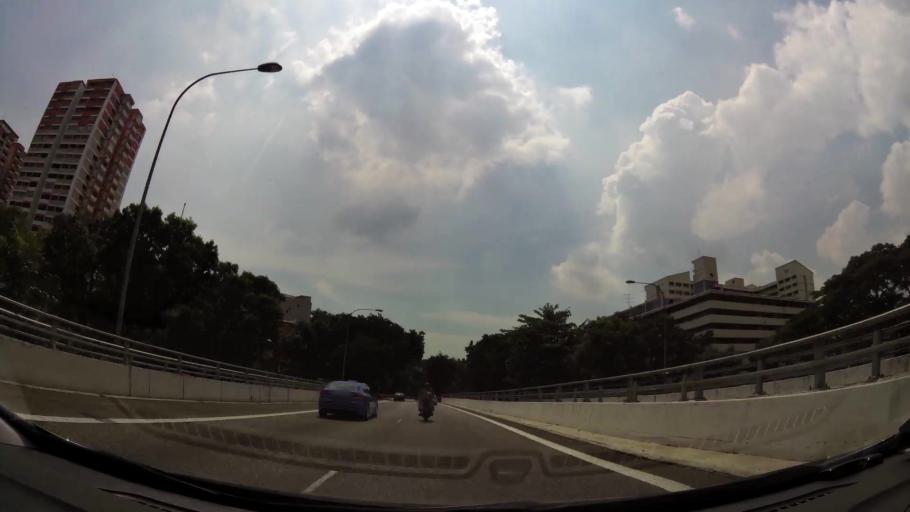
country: SG
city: Singapore
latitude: 1.2791
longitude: 103.8291
